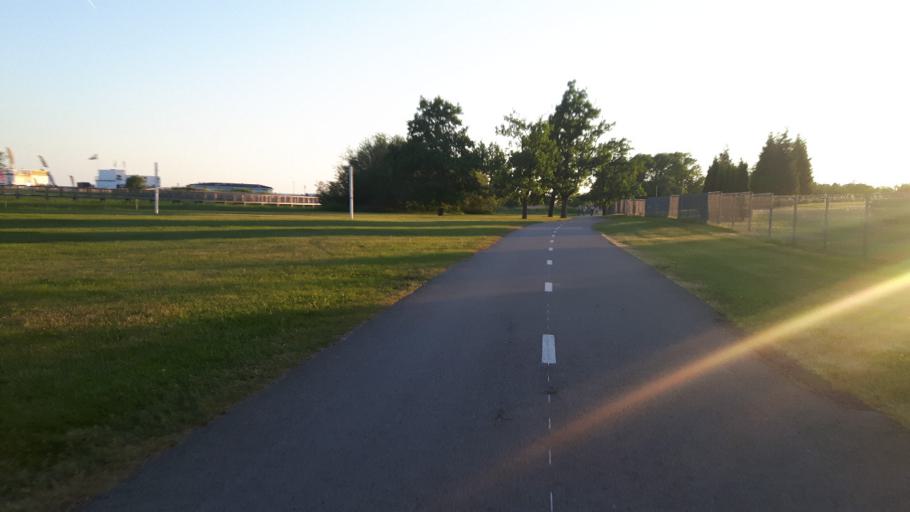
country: EE
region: Paernumaa
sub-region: Paernu linn
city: Parnu
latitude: 58.3725
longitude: 24.5116
